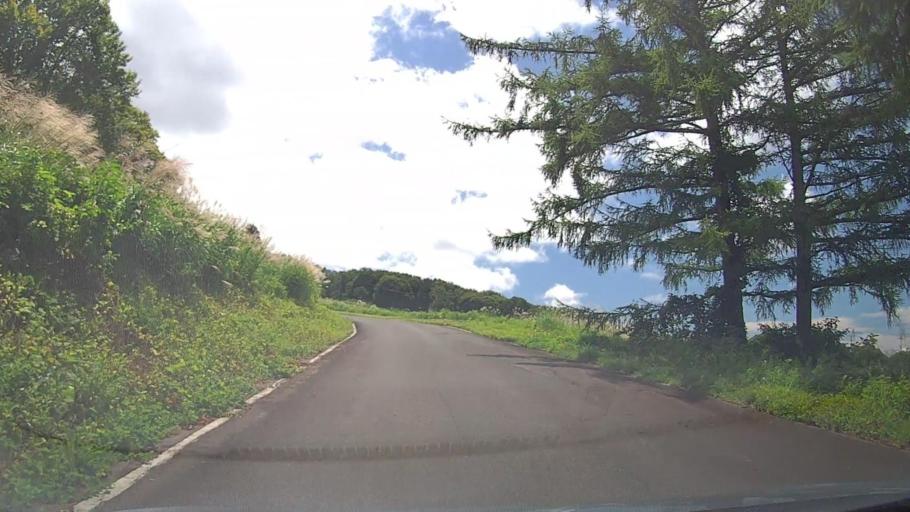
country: JP
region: Nagano
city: Iiyama
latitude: 36.9251
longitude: 138.4744
